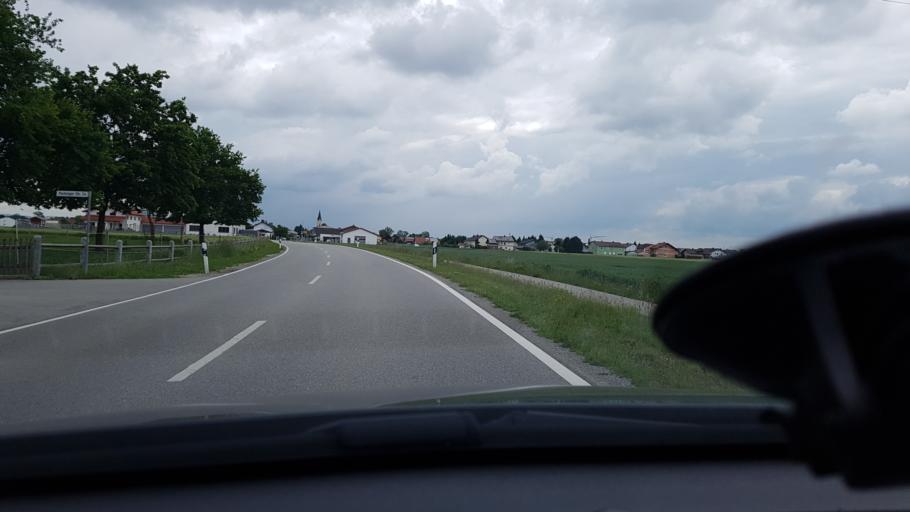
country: DE
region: Bavaria
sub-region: Lower Bavaria
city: Pocking
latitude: 48.4060
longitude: 13.3771
